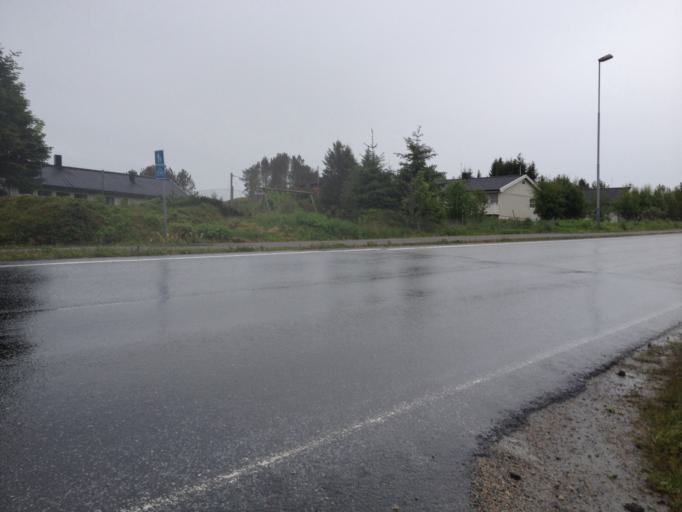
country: NO
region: Sor-Trondelag
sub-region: Froya
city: Sistranda
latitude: 63.6988
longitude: 8.8032
